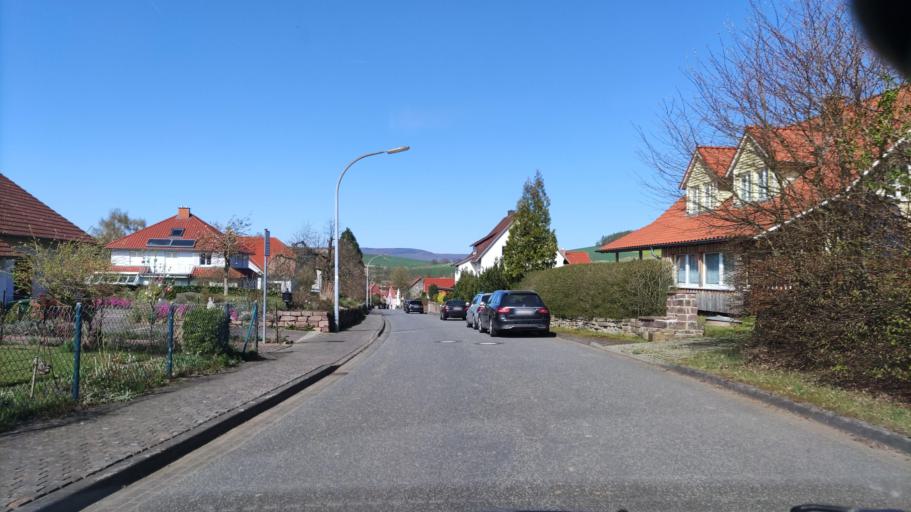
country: DE
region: Lower Saxony
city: Uslar
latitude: 51.6220
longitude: 9.6202
